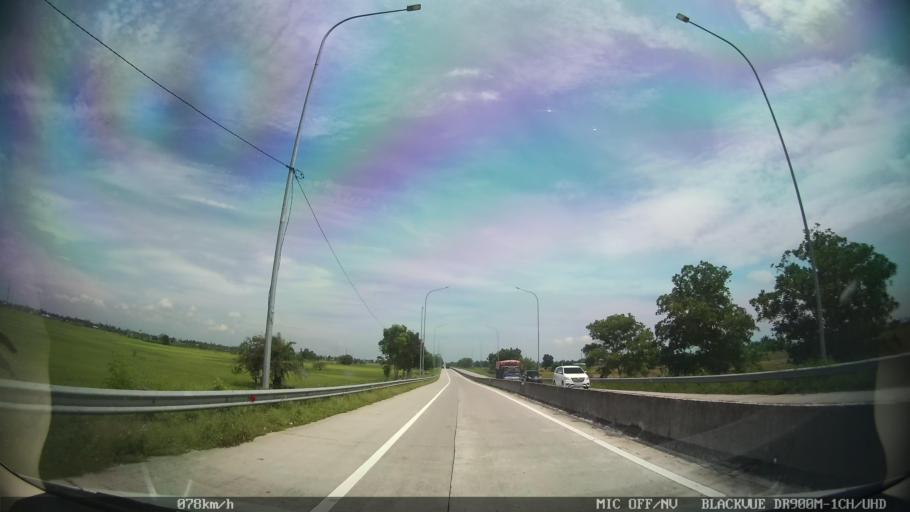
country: ID
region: North Sumatra
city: Perbaungan
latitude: 3.5421
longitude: 98.8916
